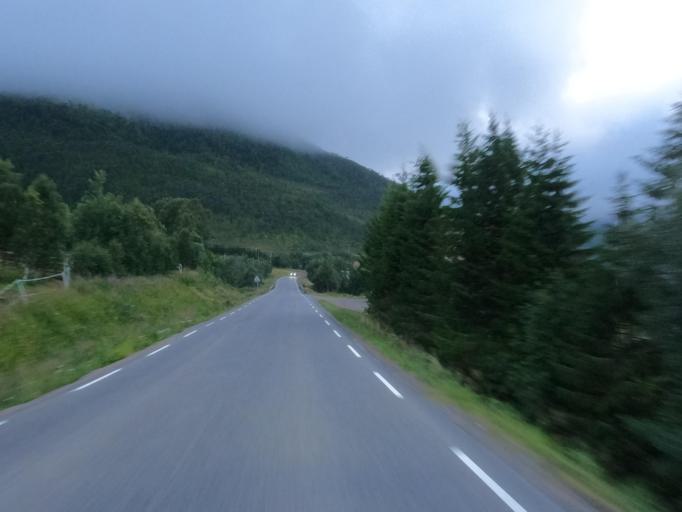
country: NO
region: Nordland
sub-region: Lodingen
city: Lodingen
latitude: 68.6030
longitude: 15.7847
